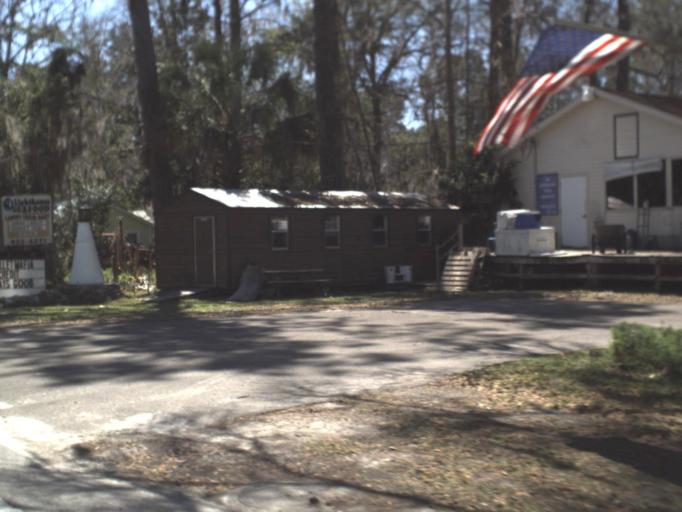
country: US
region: Florida
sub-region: Leon County
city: Woodville
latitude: 30.1607
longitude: -84.2059
